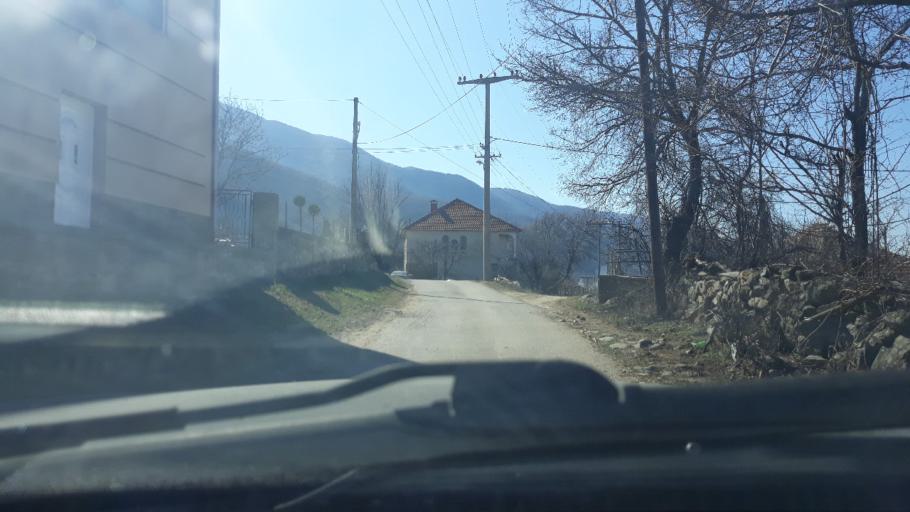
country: MK
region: Novo Selo
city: Novo Selo
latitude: 41.3770
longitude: 22.8458
